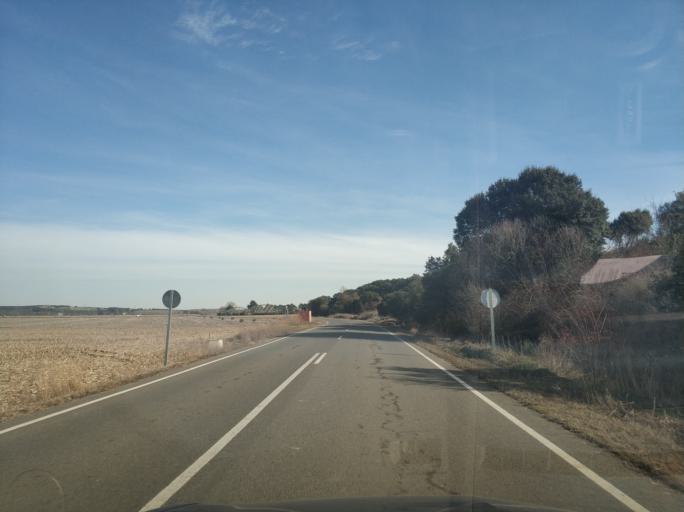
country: ES
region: Castille and Leon
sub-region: Provincia de Salamanca
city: Valverdon
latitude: 41.0365
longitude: -5.7763
